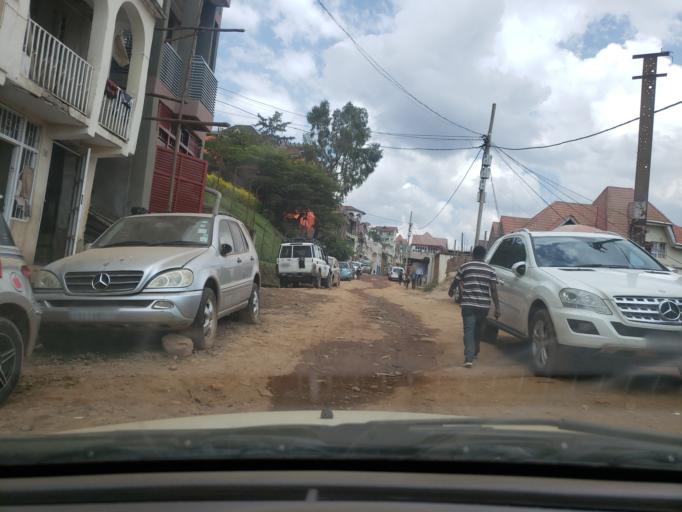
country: CD
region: South Kivu
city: Bukavu
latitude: -2.5028
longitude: 28.8643
